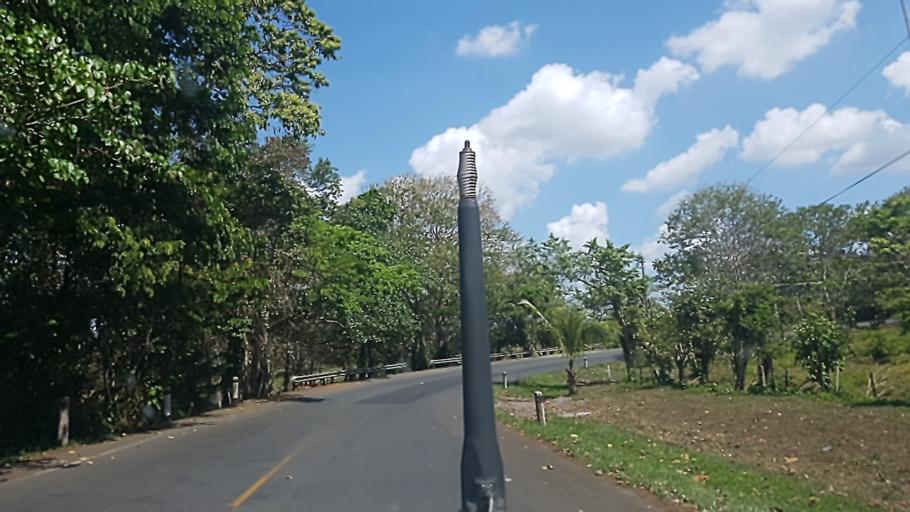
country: NI
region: Atlantico Sur
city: Muelle de los Bueyes
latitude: 11.9098
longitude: -84.6394
